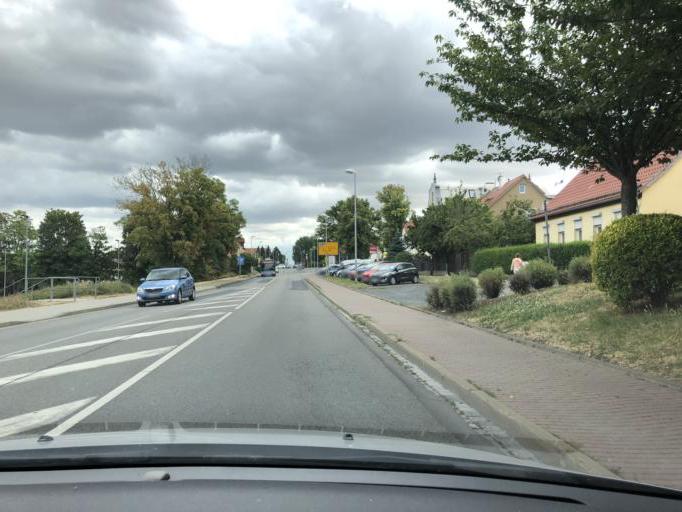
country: DE
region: Saxony-Anhalt
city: Volkstedt
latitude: 51.5231
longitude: 11.5563
